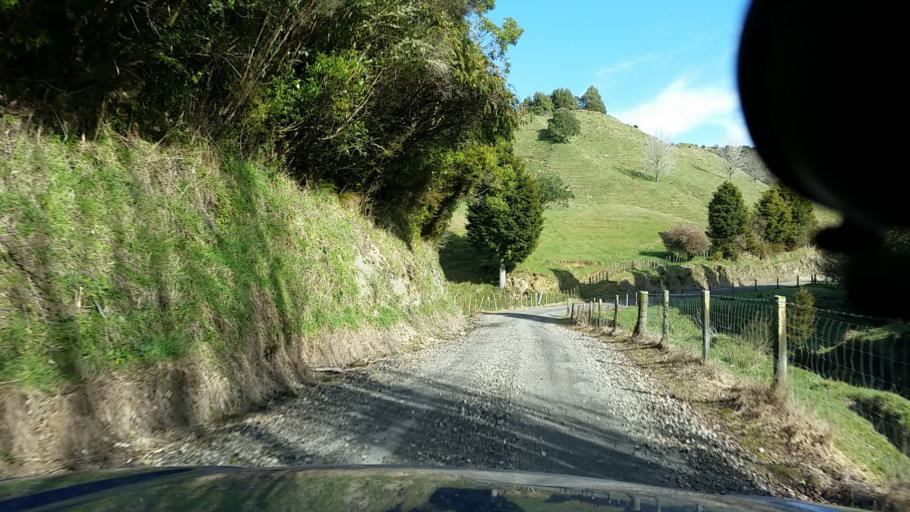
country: NZ
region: Taranaki
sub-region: New Plymouth District
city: Waitara
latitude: -39.0334
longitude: 174.7753
